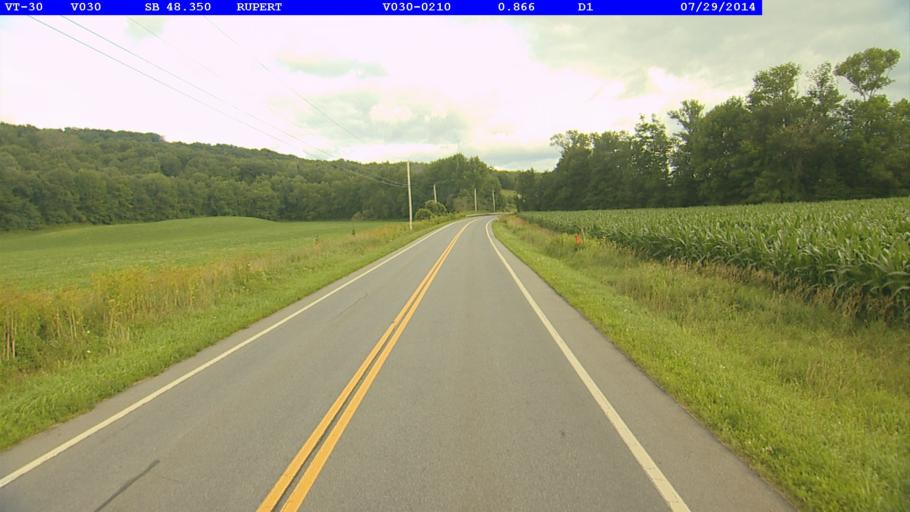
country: US
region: Vermont
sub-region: Bennington County
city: Manchester Center
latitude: 43.2827
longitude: -73.1276
